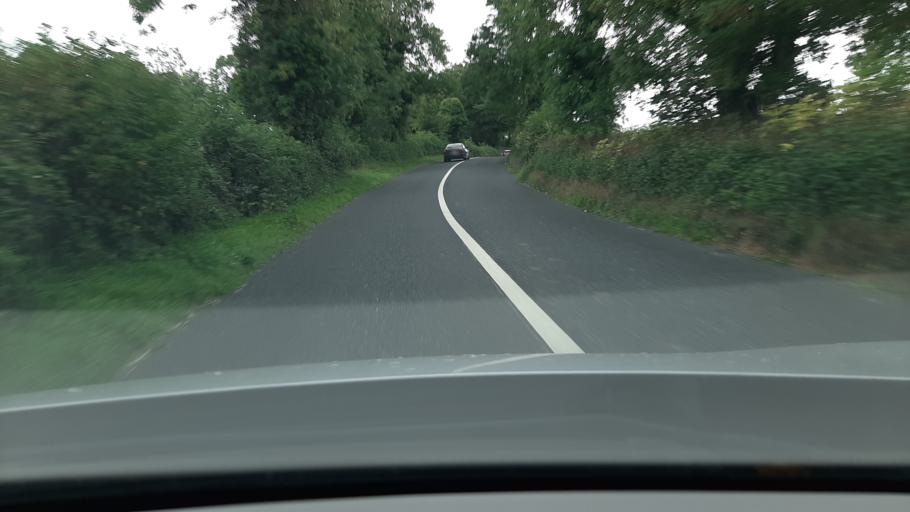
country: IE
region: Leinster
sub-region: Kildare
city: Rathangan
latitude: 53.2129
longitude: -6.9663
